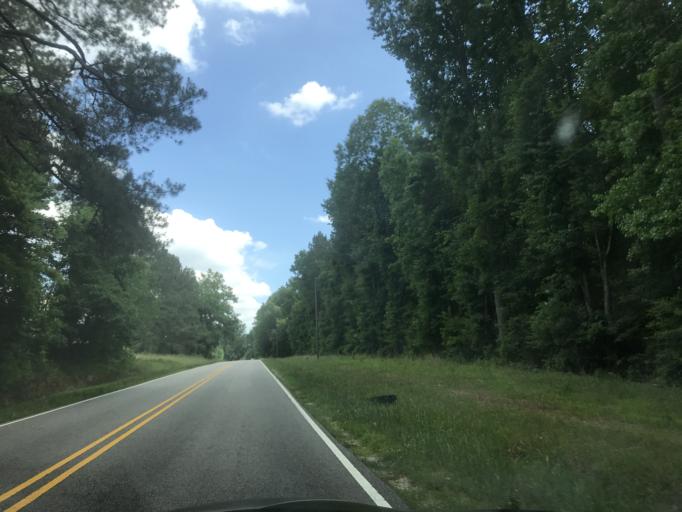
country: US
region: North Carolina
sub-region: Nash County
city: Spring Hope
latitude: 35.9295
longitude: -78.1957
